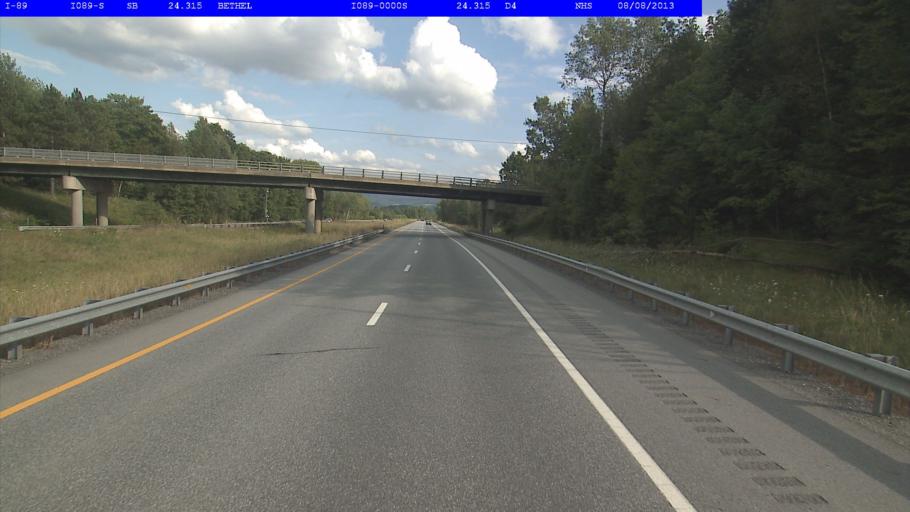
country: US
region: Vermont
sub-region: Orange County
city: Randolph
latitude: 43.8526
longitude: -72.6054
